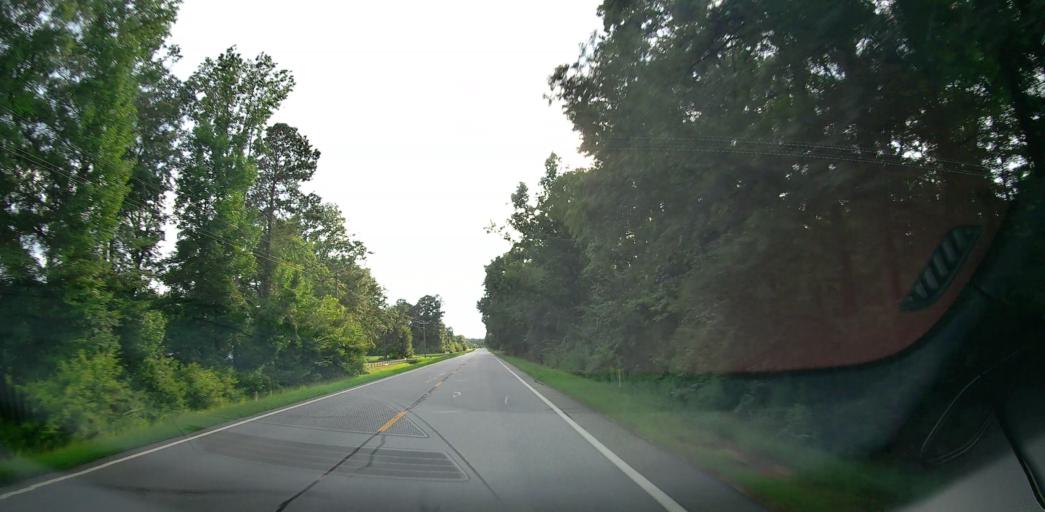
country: US
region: Georgia
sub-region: Pulaski County
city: Hawkinsville
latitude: 32.2955
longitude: -83.5502
